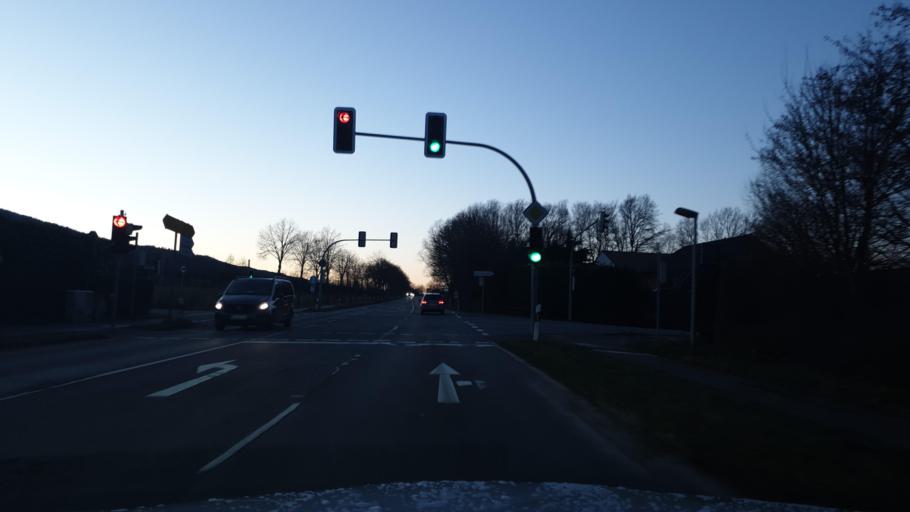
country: DE
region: North Rhine-Westphalia
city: Porta Westfalica
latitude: 52.2559
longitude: 8.8996
